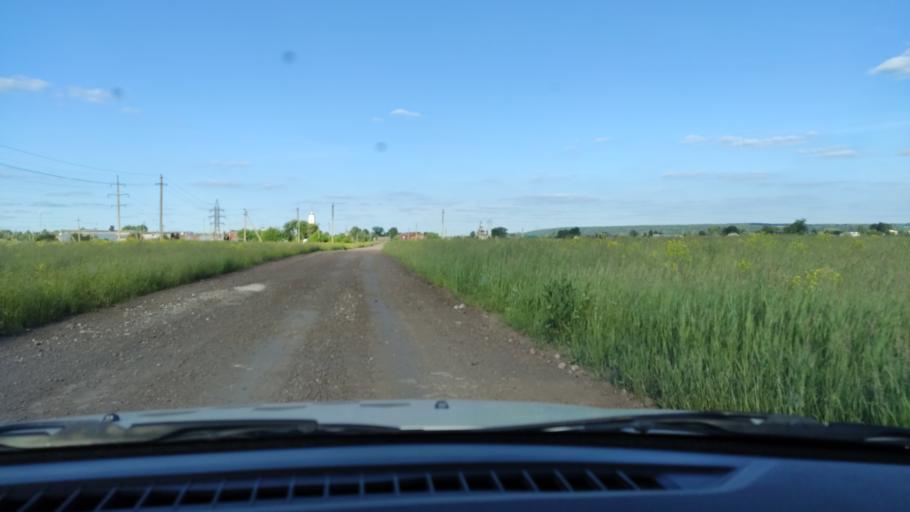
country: RU
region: Perm
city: Orda
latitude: 57.3037
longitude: 56.6416
